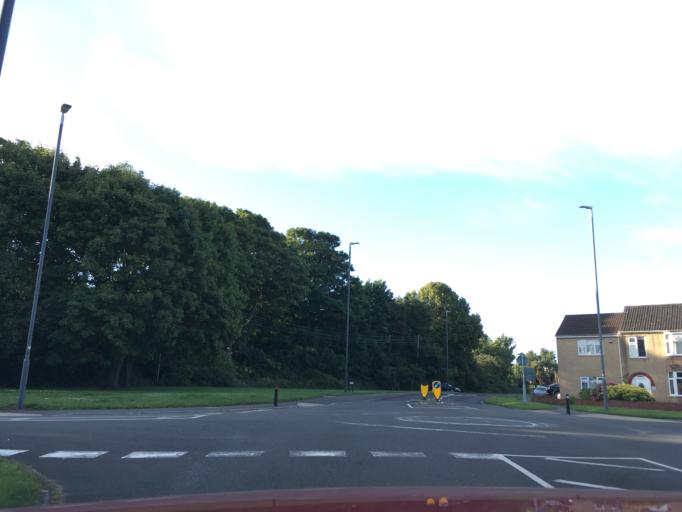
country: GB
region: England
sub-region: South Gloucestershire
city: Mangotsfield
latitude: 51.4876
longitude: -2.4848
